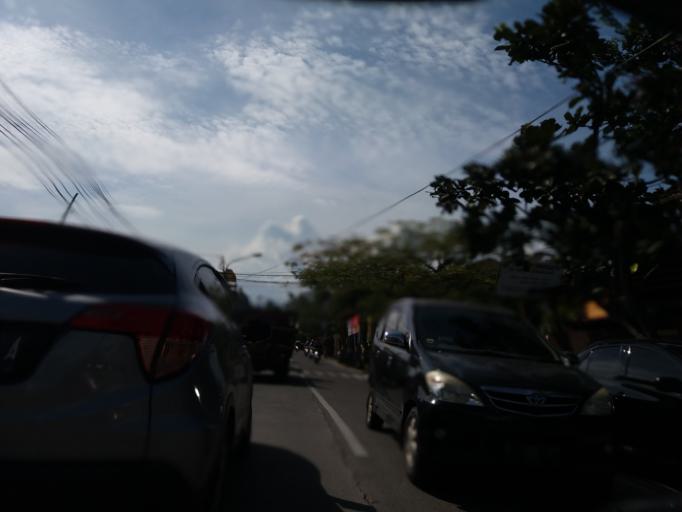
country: ID
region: West Java
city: Bandung
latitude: -6.9405
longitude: 107.6128
